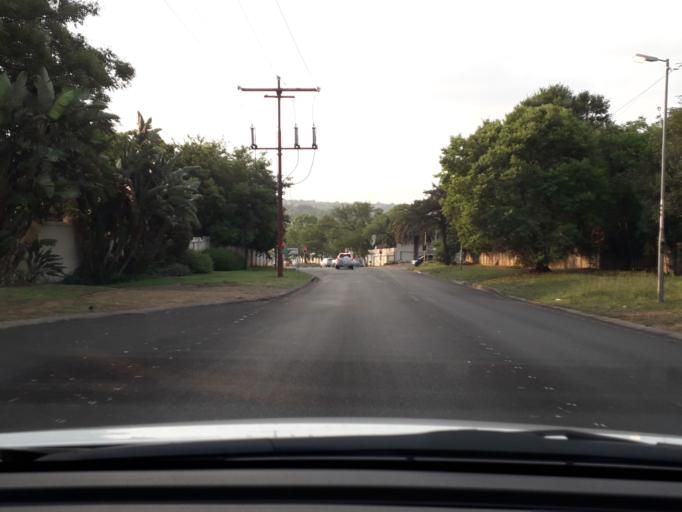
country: ZA
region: Gauteng
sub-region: City of Johannesburg Metropolitan Municipality
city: Midrand
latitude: -26.0654
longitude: 28.0544
